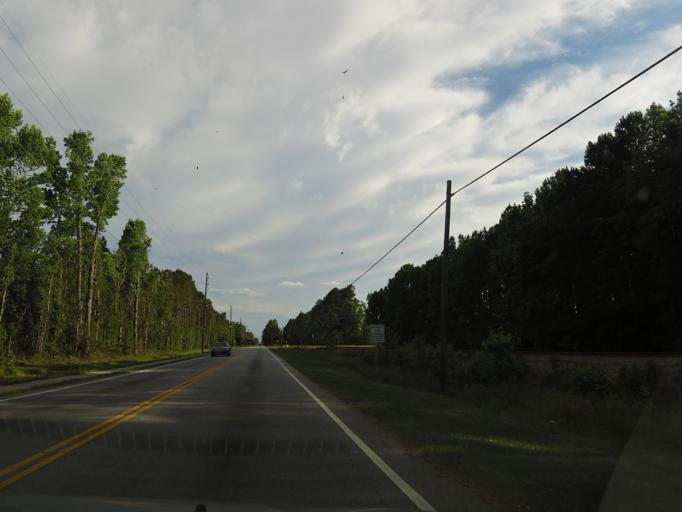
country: US
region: South Carolina
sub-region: Hampton County
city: Estill
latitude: 32.7419
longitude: -81.2416
